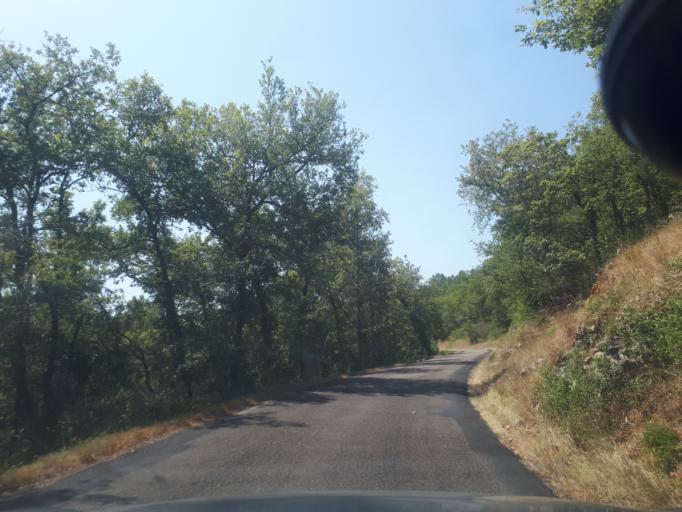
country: FR
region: Midi-Pyrenees
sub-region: Departement du Lot
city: Souillac
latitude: 44.8444
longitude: 1.4015
